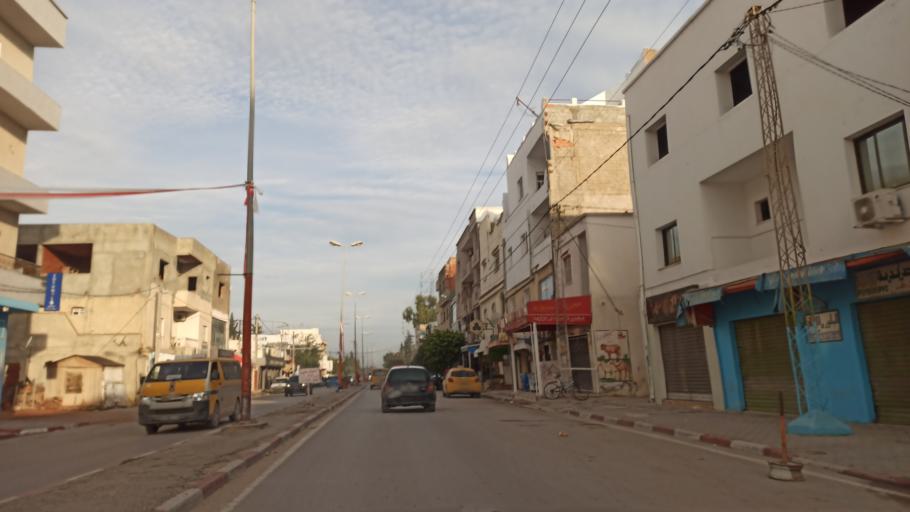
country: TN
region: Ariana
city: Ariana
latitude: 36.8663
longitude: 10.2515
